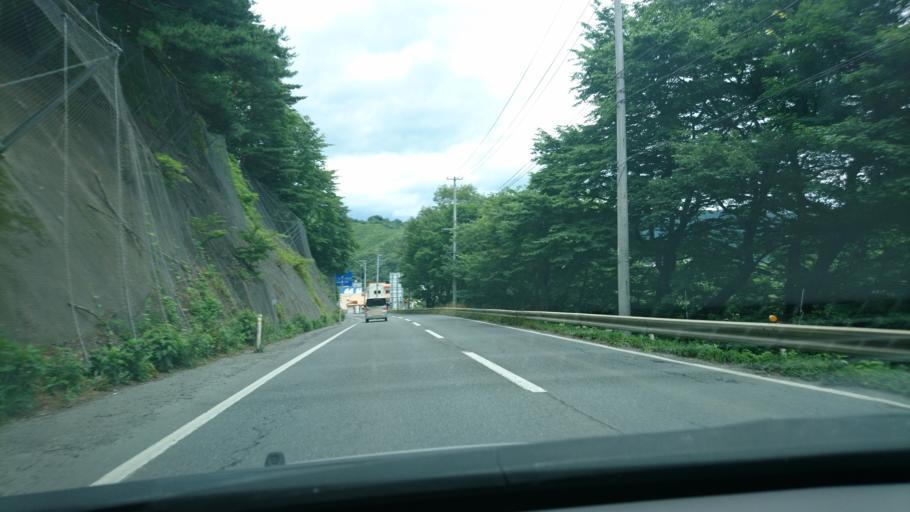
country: JP
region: Iwate
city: Otsuchi
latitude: 39.3511
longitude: 141.8931
